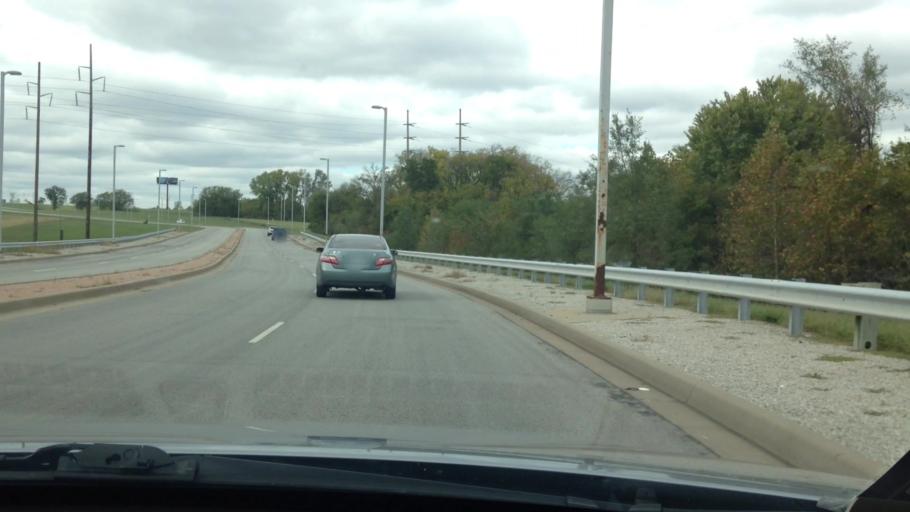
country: US
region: Missouri
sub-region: Platte County
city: Weatherby Lake
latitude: 39.3202
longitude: -94.7008
